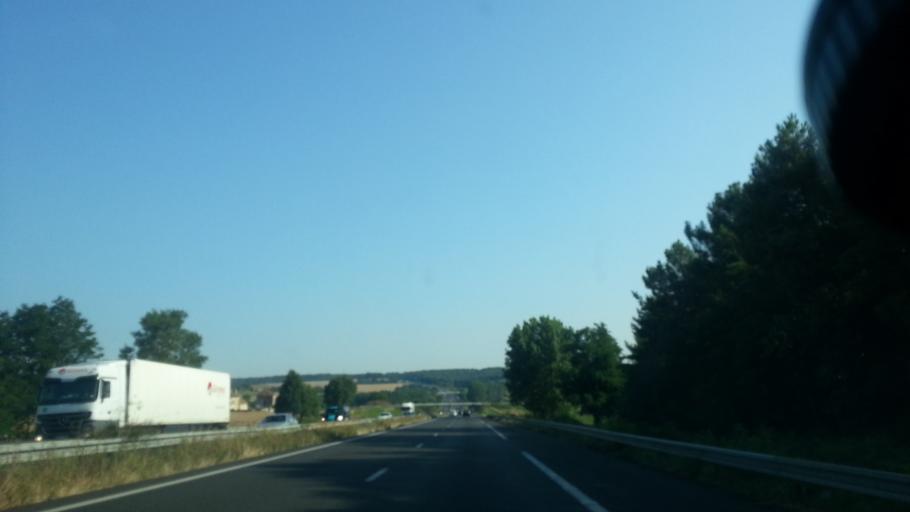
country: FR
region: Poitou-Charentes
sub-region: Departement de la Vienne
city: Dange-Saint-Romain
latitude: 46.9389
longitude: 0.5453
